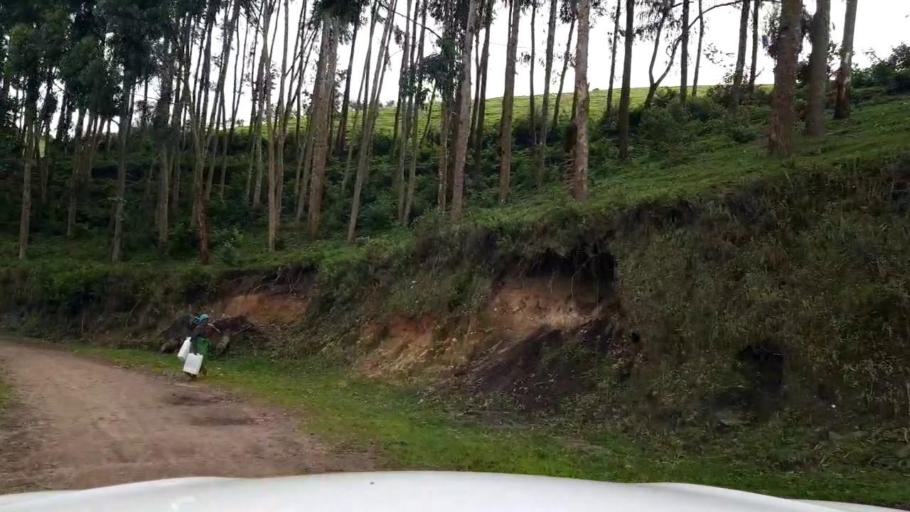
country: RW
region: Western Province
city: Gisenyi
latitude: -1.6863
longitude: 29.4184
